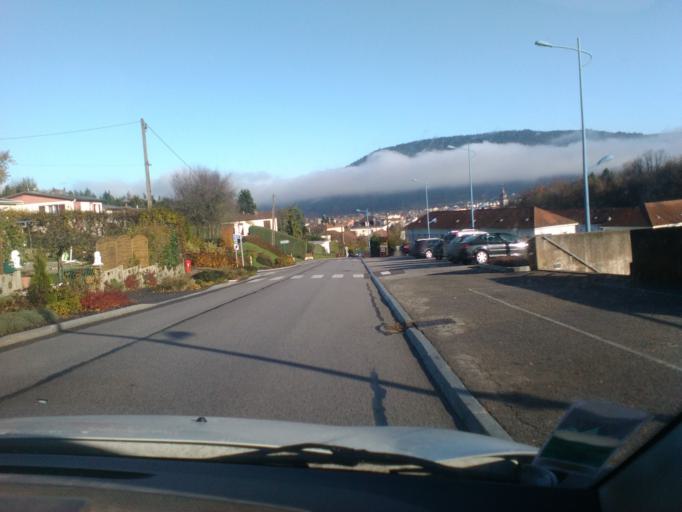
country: FR
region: Lorraine
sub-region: Departement des Vosges
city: Remiremont
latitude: 48.0088
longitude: 6.5816
